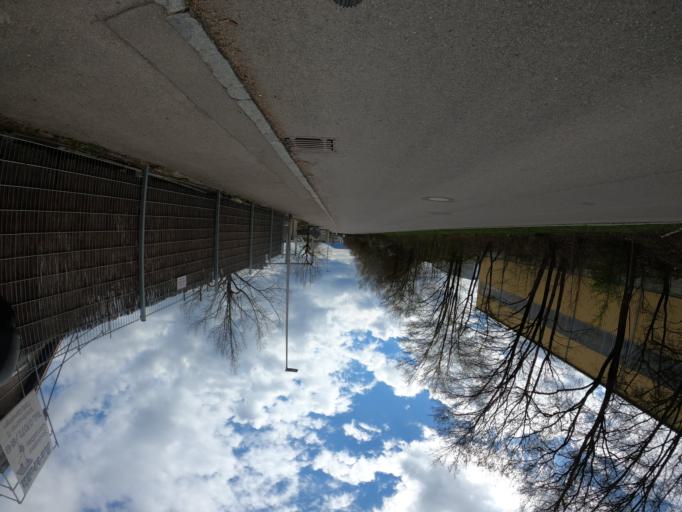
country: DE
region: Baden-Wuerttemberg
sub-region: Tuebingen Region
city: Nehren
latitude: 48.4341
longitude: 9.0789
